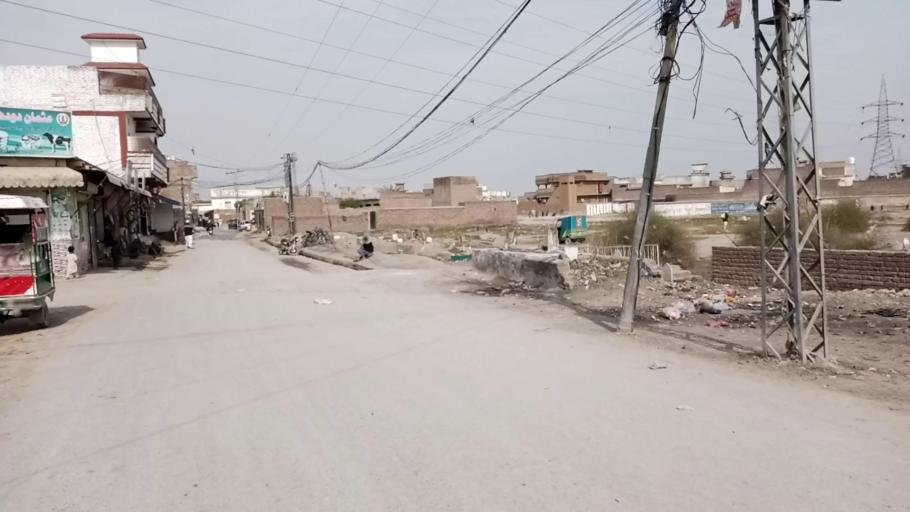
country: PK
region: Khyber Pakhtunkhwa
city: Peshawar
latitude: 33.9862
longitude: 71.4682
